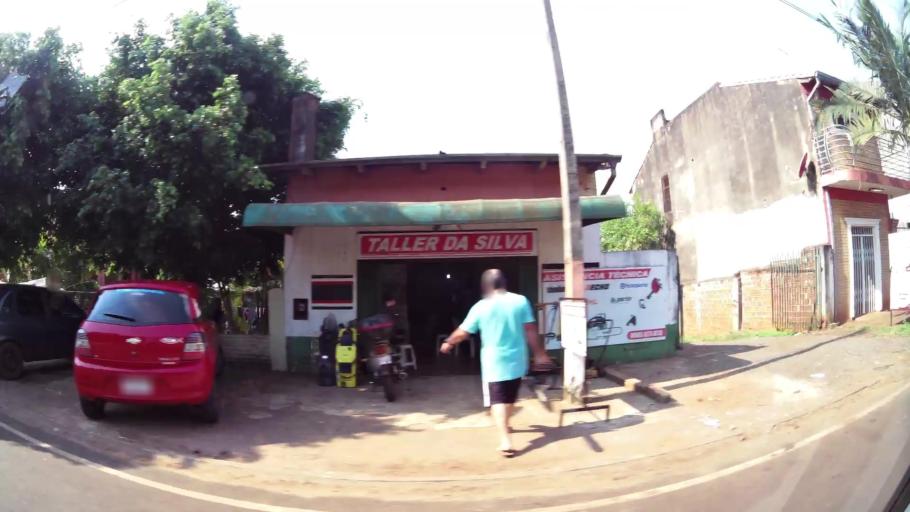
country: PY
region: Alto Parana
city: Ciudad del Este
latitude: -25.5069
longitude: -54.6345
